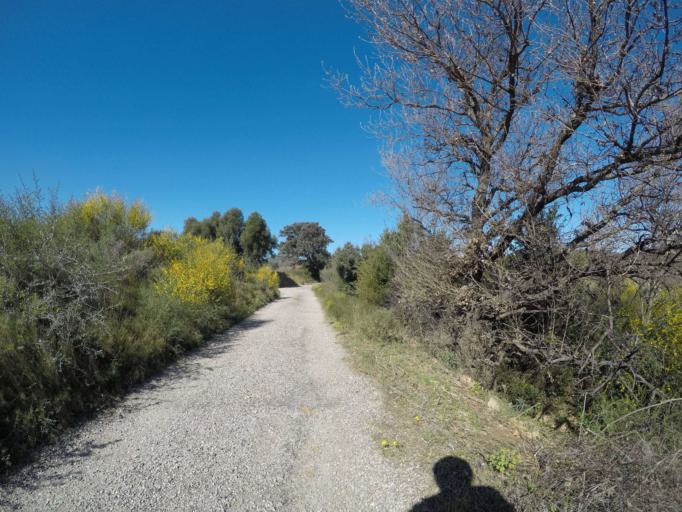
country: FR
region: Languedoc-Roussillon
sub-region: Departement des Pyrenees-Orientales
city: Millas
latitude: 42.7069
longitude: 2.6707
